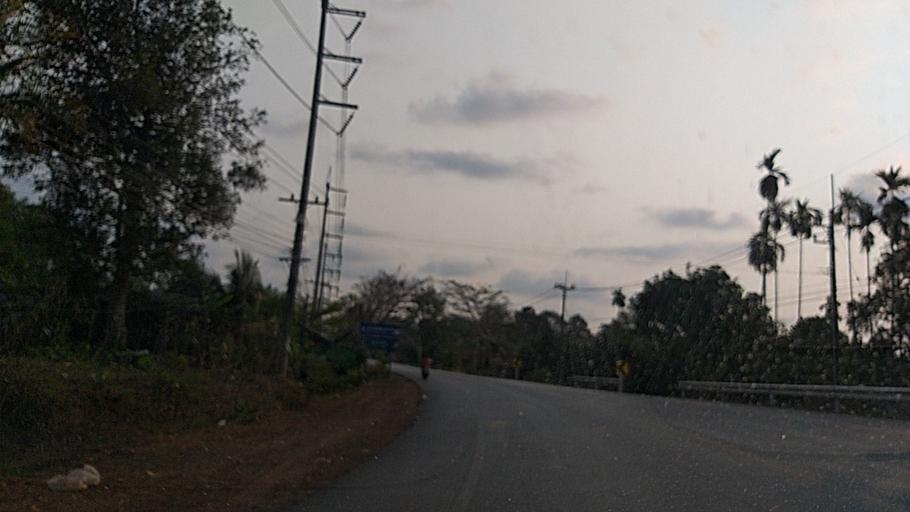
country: TH
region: Trat
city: Khao Saming
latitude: 12.2968
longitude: 102.3346
